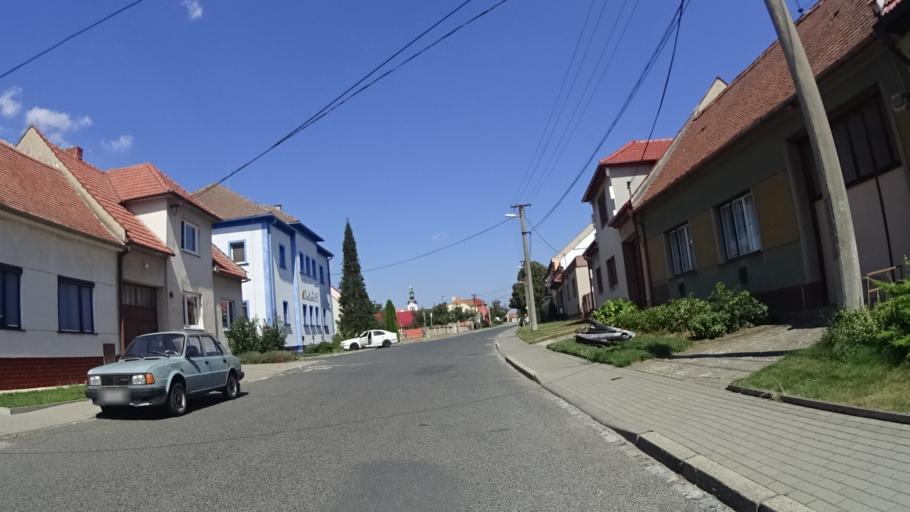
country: CZ
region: South Moravian
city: Vnorovy
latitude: 48.9264
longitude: 17.3441
